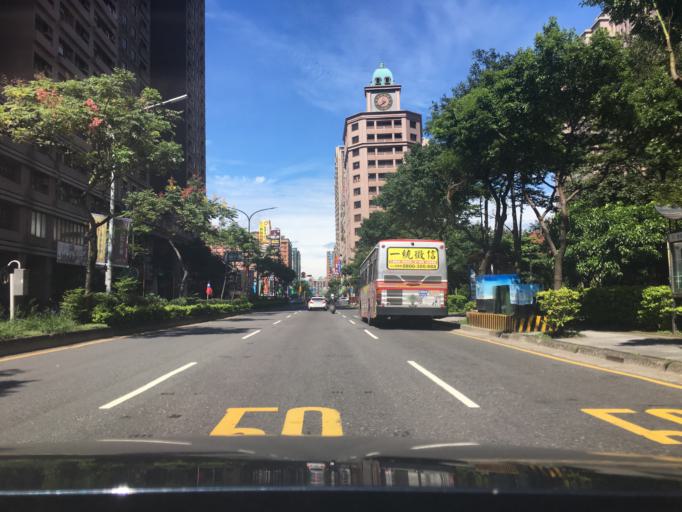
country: TW
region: Taiwan
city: Taoyuan City
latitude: 25.0419
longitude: 121.2953
